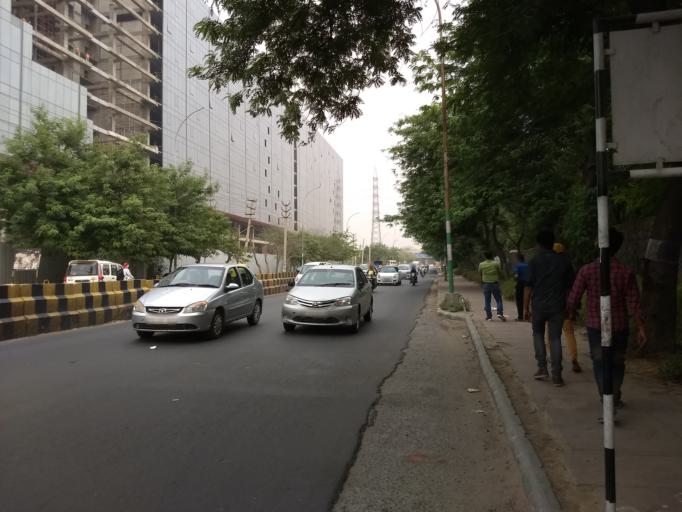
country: IN
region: Haryana
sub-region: Gurgaon
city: Gurgaon
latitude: 28.5033
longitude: 77.0882
